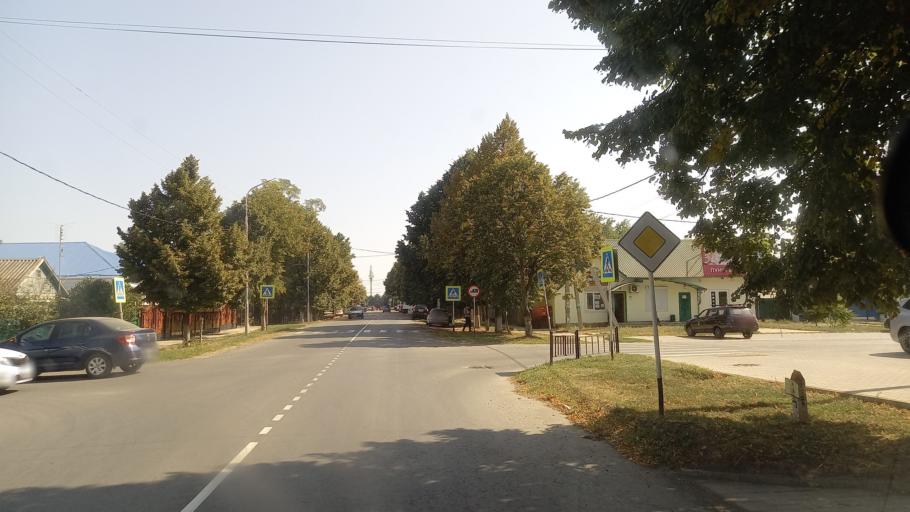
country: RU
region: Krasnodarskiy
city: Bryukhovetskaya
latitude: 45.8023
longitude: 38.9997
